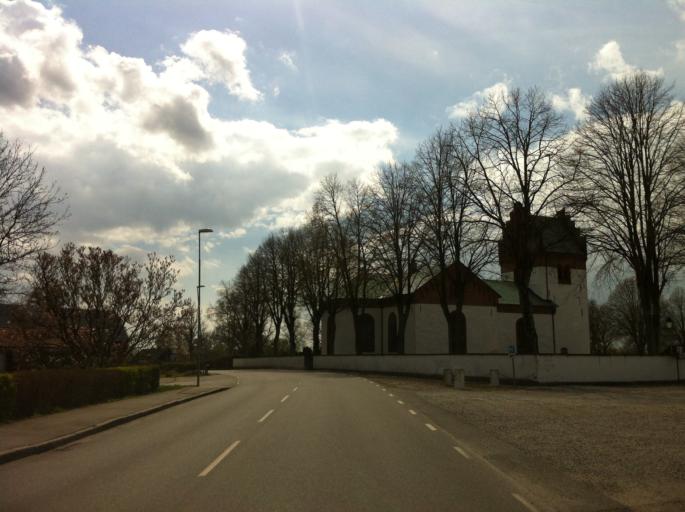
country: SE
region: Skane
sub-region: Kavlinge Kommun
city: Kaevlinge
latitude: 55.8055
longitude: 13.1551
